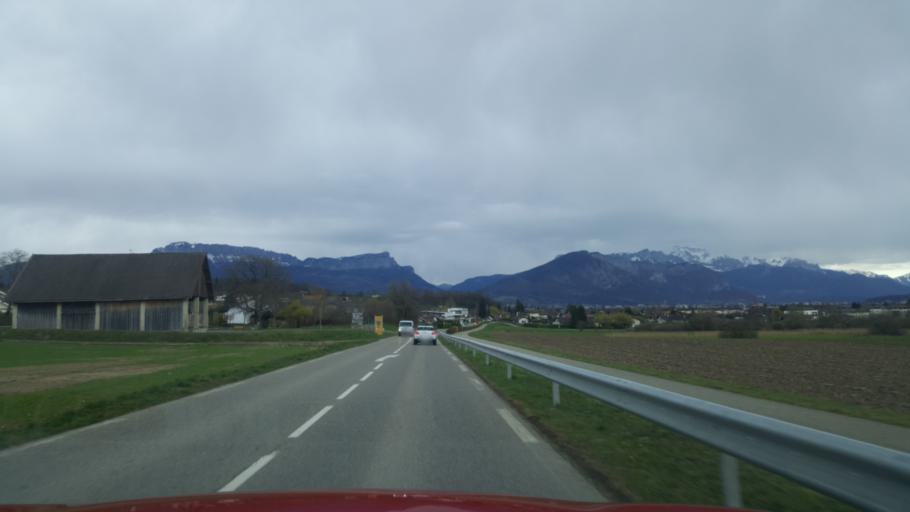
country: FR
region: Rhone-Alpes
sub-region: Departement de la Haute-Savoie
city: Epagny
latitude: 45.9446
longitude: 6.0784
